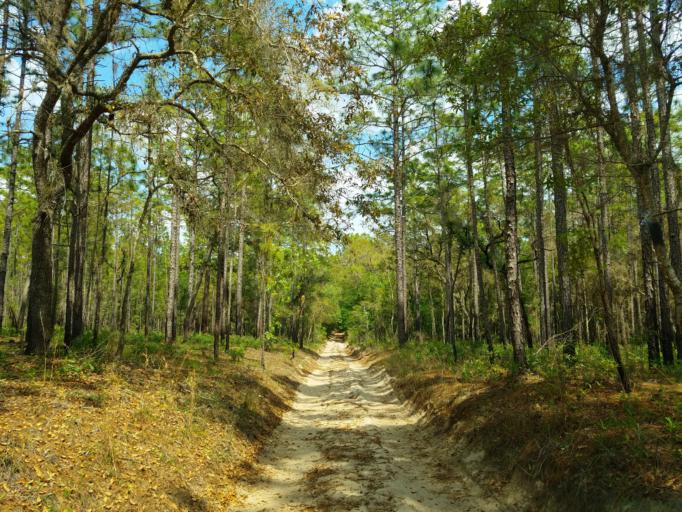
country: US
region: Florida
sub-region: Hernando County
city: Hill 'n Dale
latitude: 28.5502
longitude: -82.2743
